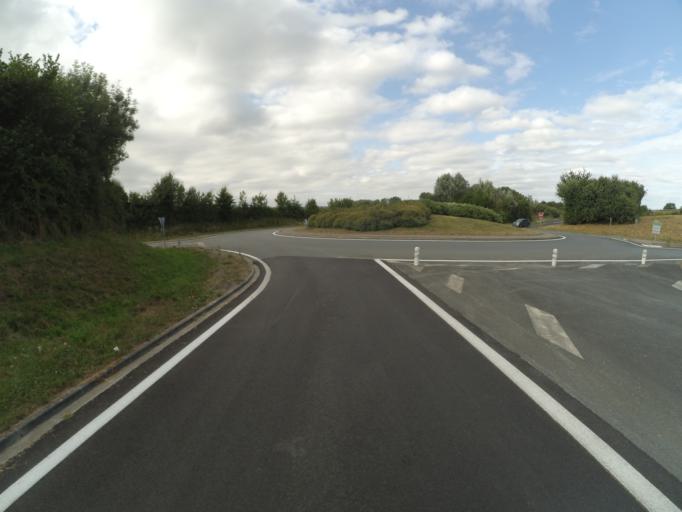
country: FR
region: Pays de la Loire
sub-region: Departement de Maine-et-Loire
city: Vezins
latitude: 47.1149
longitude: -0.7306
